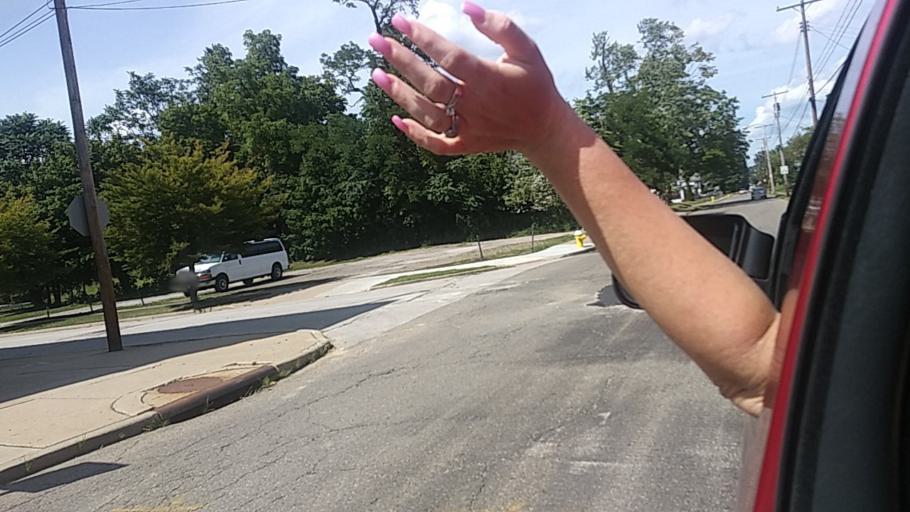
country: US
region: Ohio
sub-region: Summit County
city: Akron
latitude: 41.0856
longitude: -81.5506
